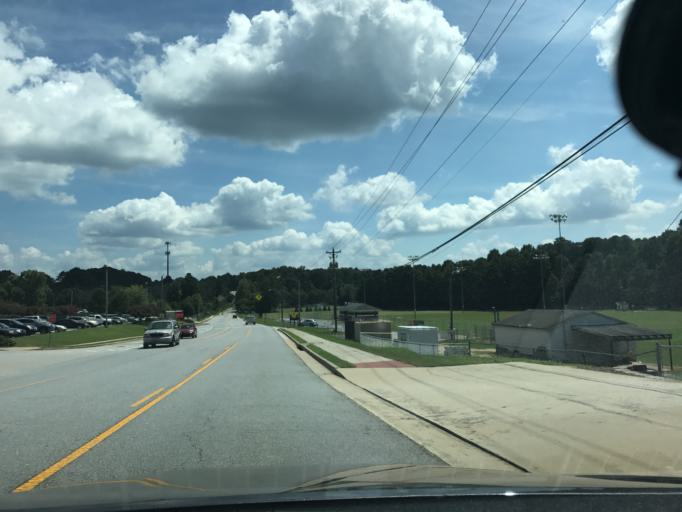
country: US
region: Georgia
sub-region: Gwinnett County
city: Mountain Park
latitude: 33.8597
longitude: -84.1164
